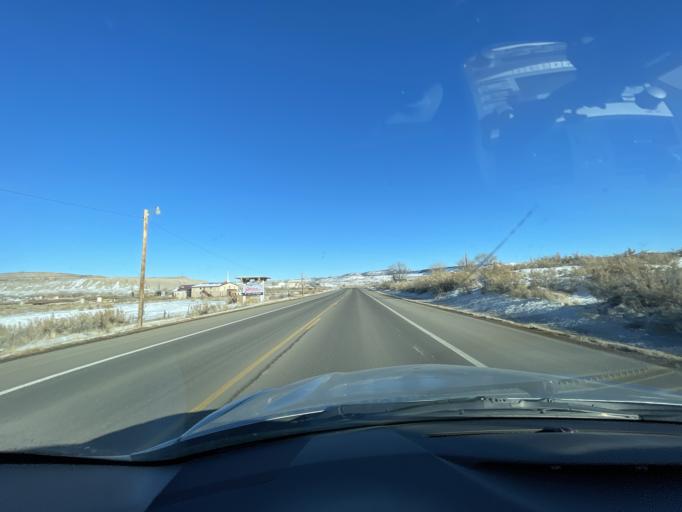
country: US
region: Colorado
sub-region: Rio Blanco County
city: Rangely
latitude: 40.0876
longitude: -108.7817
